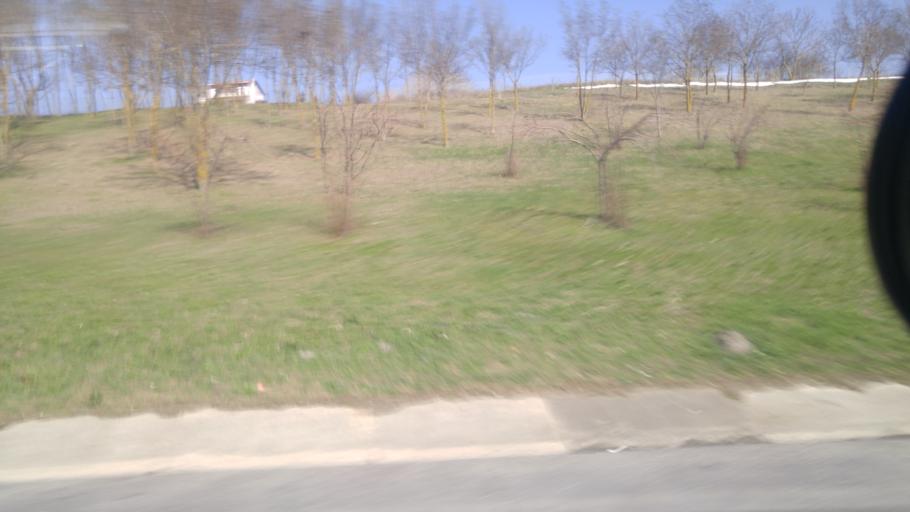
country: TR
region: Istanbul
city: Celaliye
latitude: 41.0539
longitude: 28.4293
